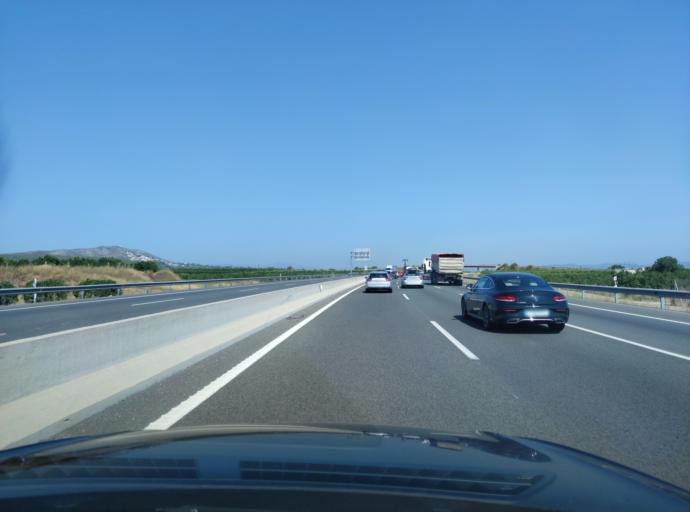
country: ES
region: Valencia
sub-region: Provincia de Valencia
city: Torrent
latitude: 39.4245
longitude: -0.5220
